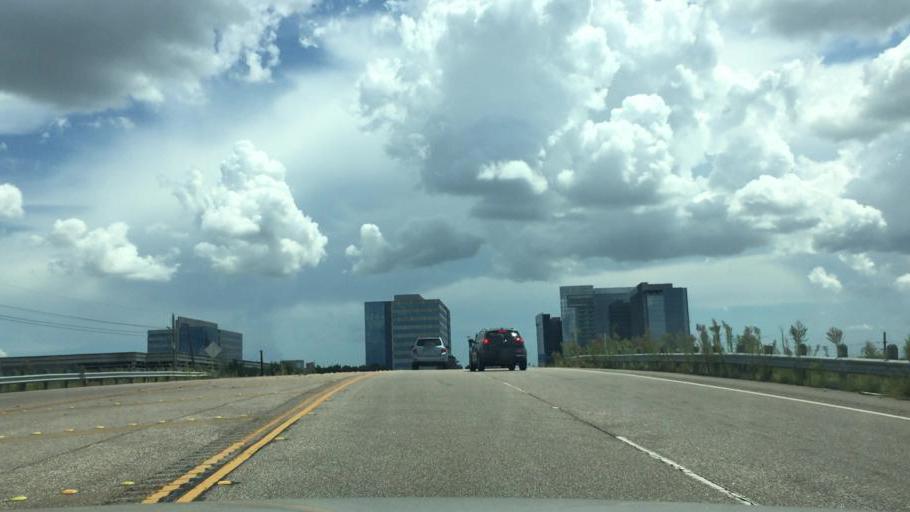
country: US
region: Texas
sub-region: Harris County
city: Bunker Hill Village
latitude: 29.7910
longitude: -95.6167
